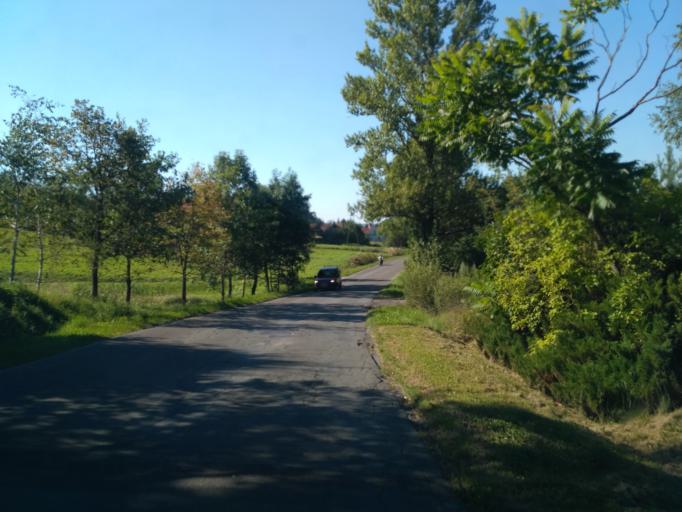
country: PL
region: Subcarpathian Voivodeship
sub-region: Powiat strzyzowski
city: Wysoka Strzyzowska
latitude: 49.8357
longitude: 21.7399
